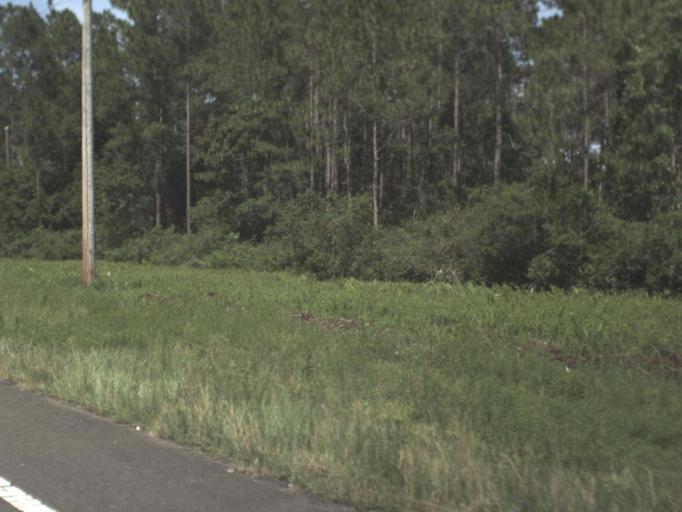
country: US
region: Florida
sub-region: Gilchrist County
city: Trenton
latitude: 29.6672
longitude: -82.7772
